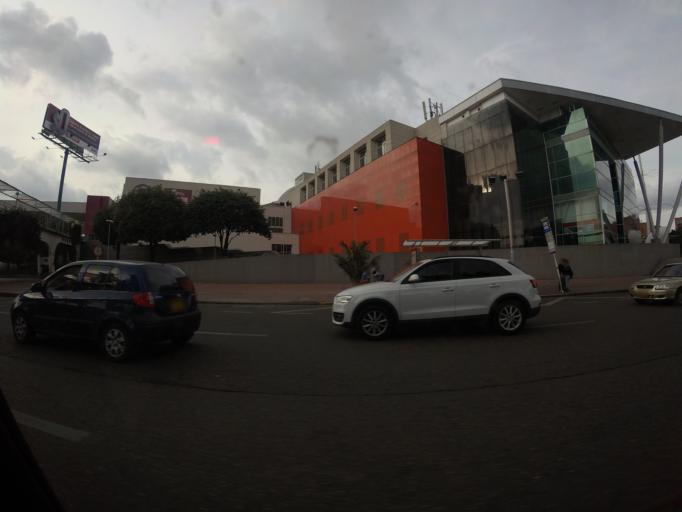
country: CO
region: Bogota D.C.
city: Barrio San Luis
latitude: 4.7115
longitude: -74.0712
